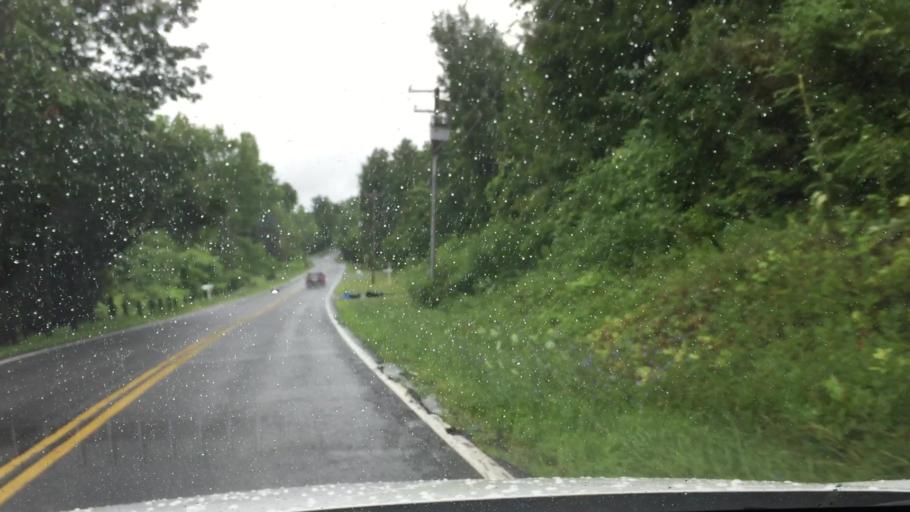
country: US
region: Massachusetts
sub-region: Berkshire County
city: Lenox
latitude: 42.4123
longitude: -73.3131
